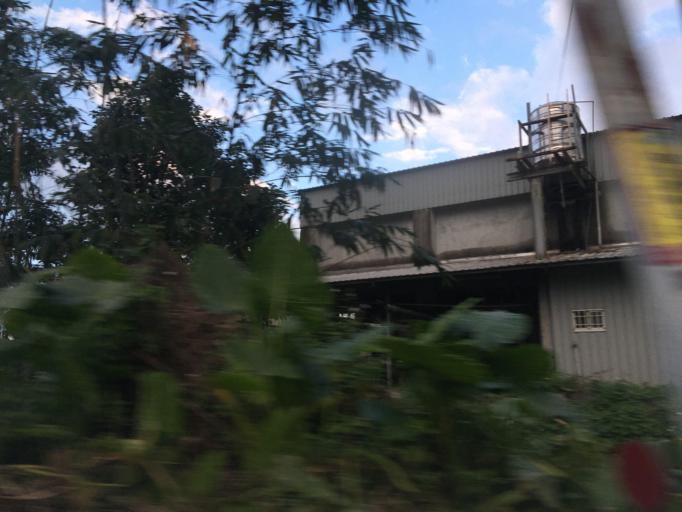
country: TW
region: Taiwan
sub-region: Yilan
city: Yilan
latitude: 24.7501
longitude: 121.7242
